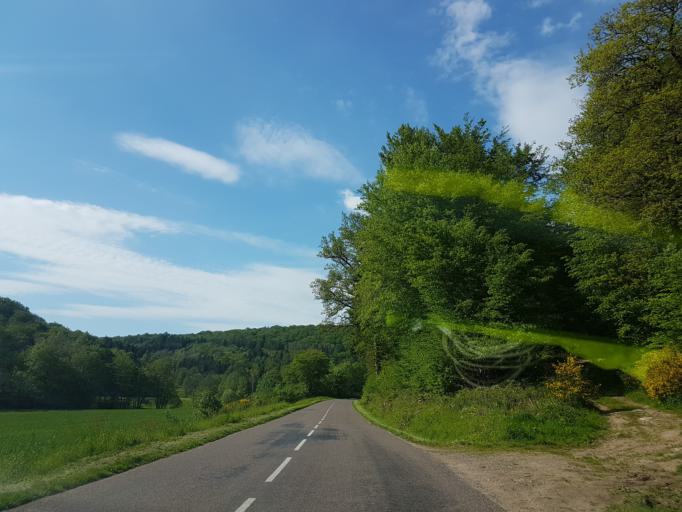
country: FR
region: Franche-Comte
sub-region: Departement de la Haute-Saone
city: Froideconche
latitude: 47.8528
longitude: 6.4797
